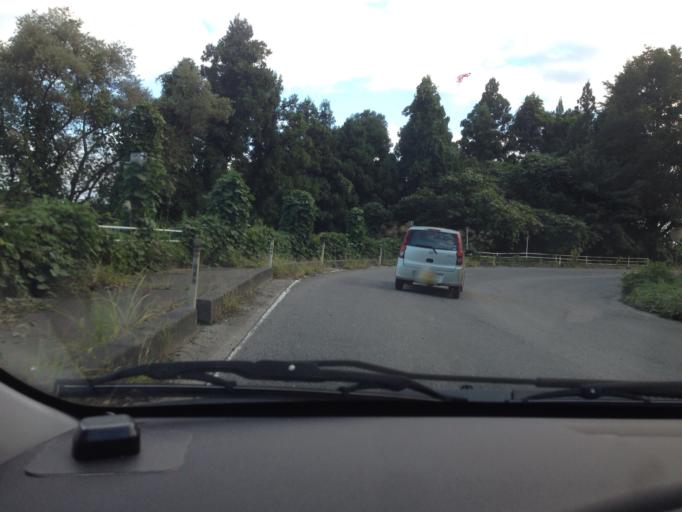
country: JP
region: Fukushima
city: Kitakata
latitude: 37.5751
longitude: 139.7617
